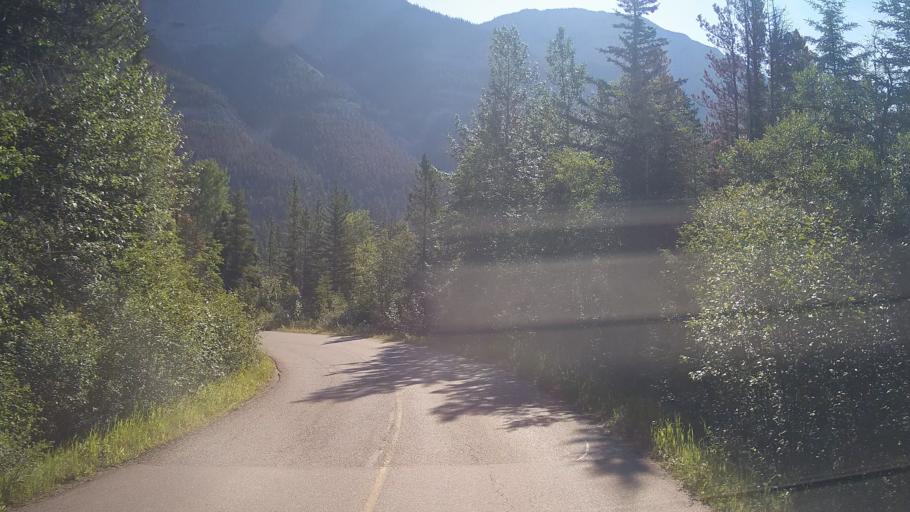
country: CA
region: Alberta
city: Hinton
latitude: 53.1770
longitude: -117.8416
